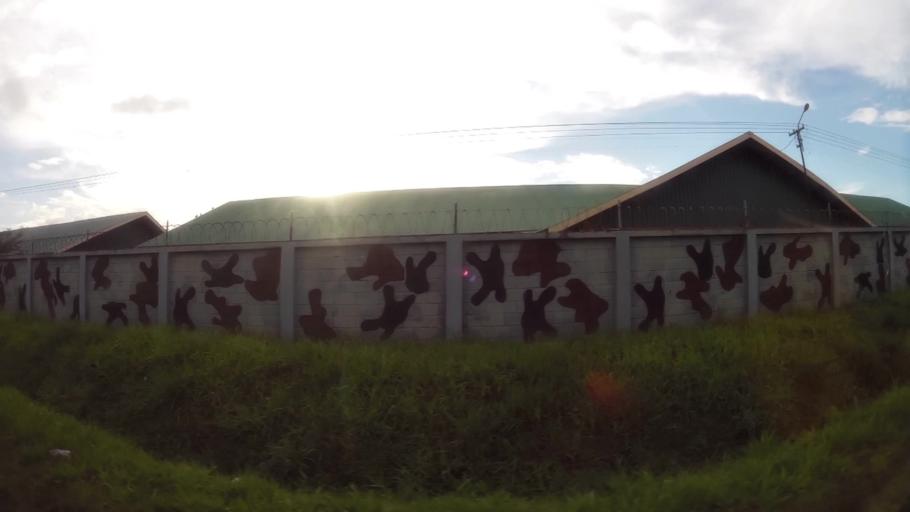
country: SR
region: Paramaribo
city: Paramaribo
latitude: 5.8259
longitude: -55.1767
